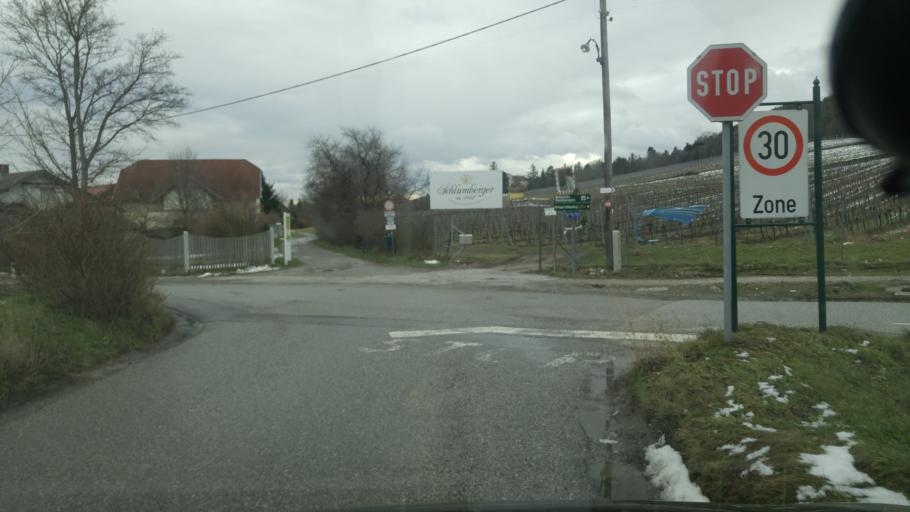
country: AT
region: Lower Austria
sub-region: Politischer Bezirk Baden
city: Bad Voslau
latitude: 47.9746
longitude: 16.2099
